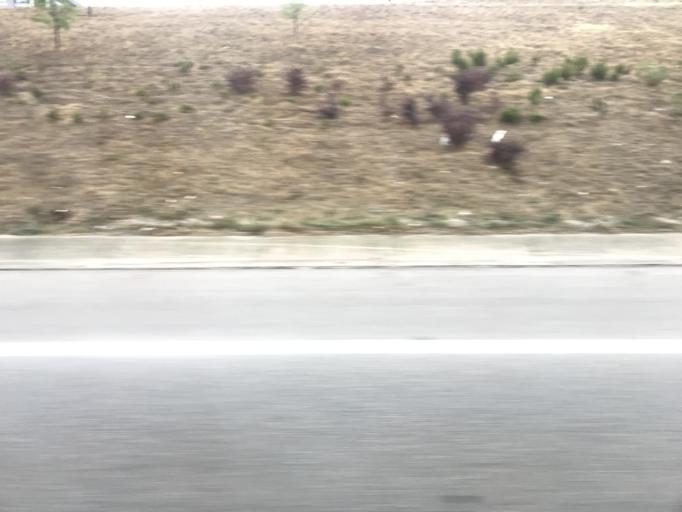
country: TR
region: Bursa
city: Niluefer
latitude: 40.2606
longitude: 28.9332
